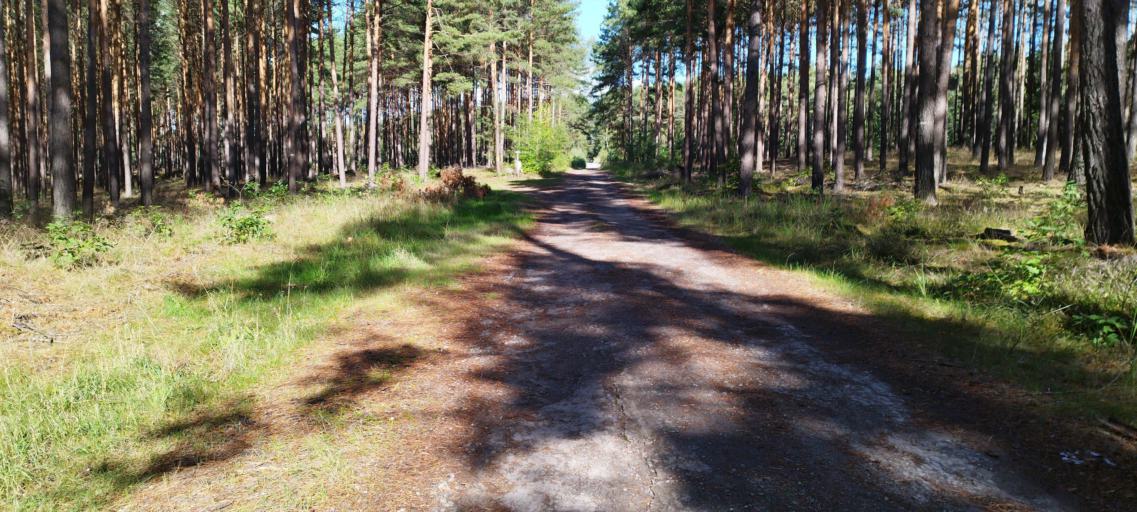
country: DE
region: Brandenburg
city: Lawitz
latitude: 52.1088
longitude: 14.5483
